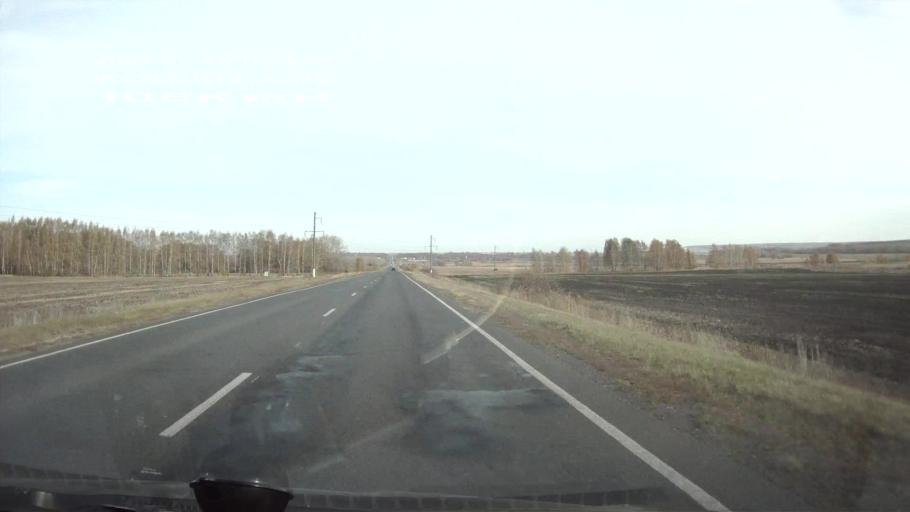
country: RU
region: Mordoviya
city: Atyashevo
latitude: 54.5438
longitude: 45.9411
